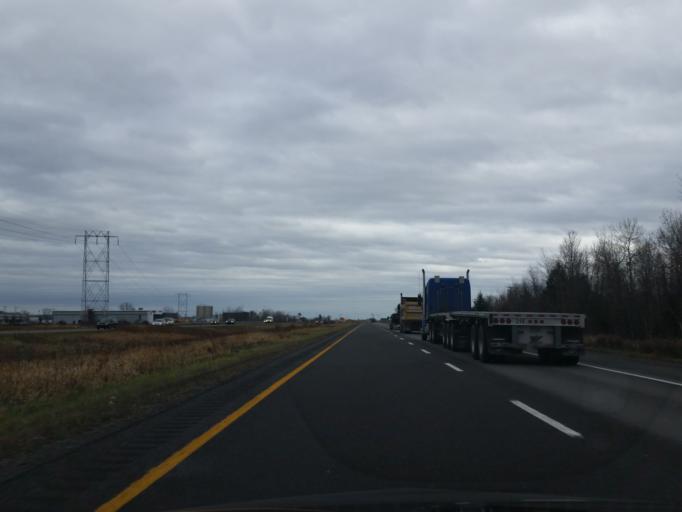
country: CA
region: Quebec
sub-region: Outaouais
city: Gatineau
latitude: 45.5117
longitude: -75.5806
